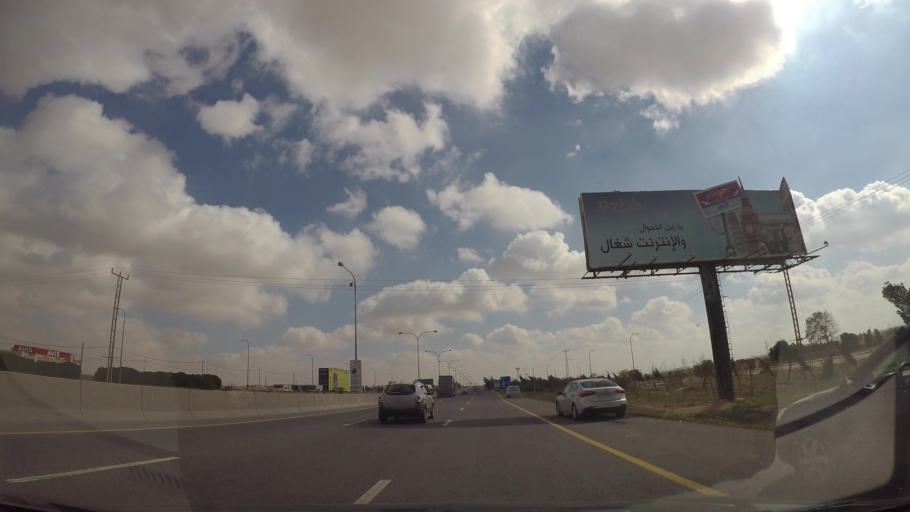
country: JO
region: Amman
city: Al Jizah
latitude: 31.7274
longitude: 35.9457
